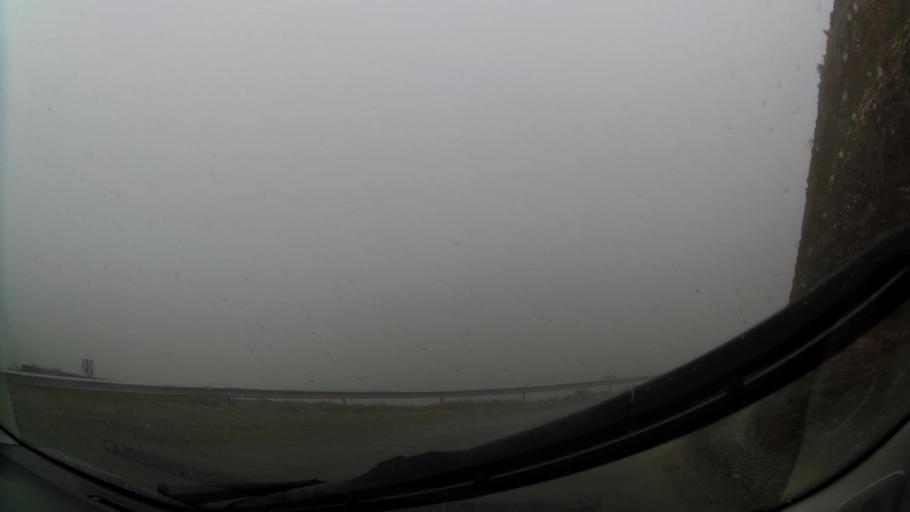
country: MA
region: Oriental
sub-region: Nador
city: Boudinar
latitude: 35.1052
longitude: -3.5561
